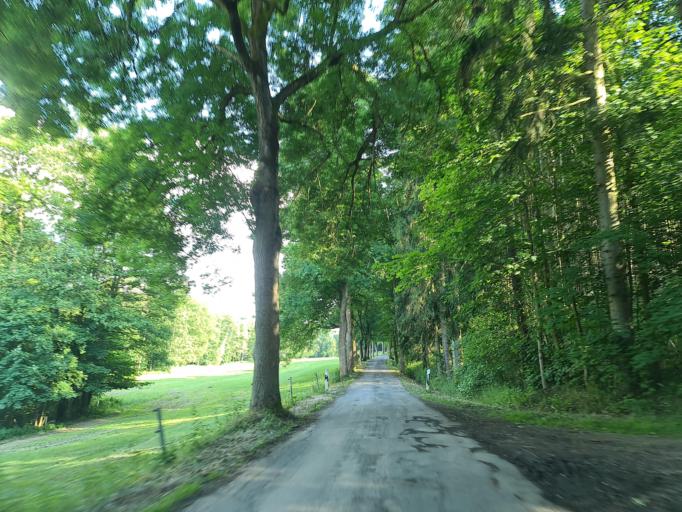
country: DE
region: Saxony
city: Bosenbrunn
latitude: 50.4075
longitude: 12.0945
